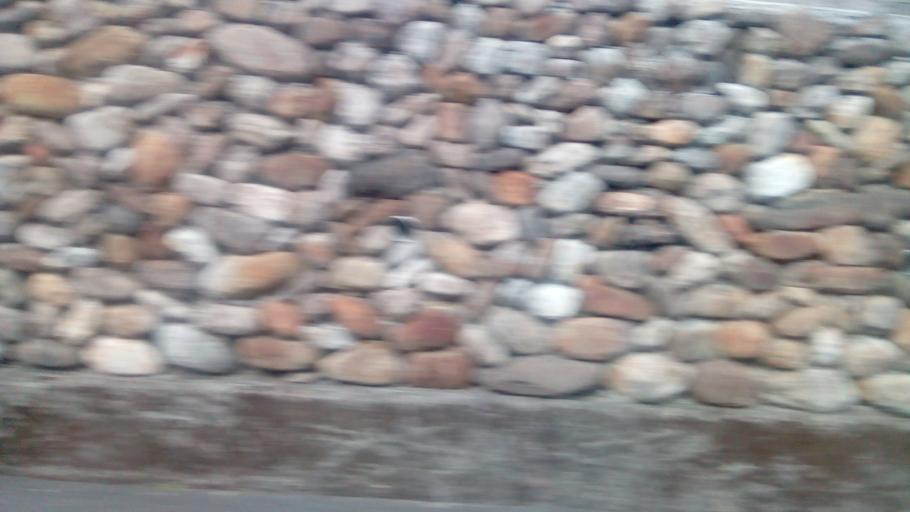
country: TW
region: Taiwan
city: Daxi
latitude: 24.4634
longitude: 121.3974
